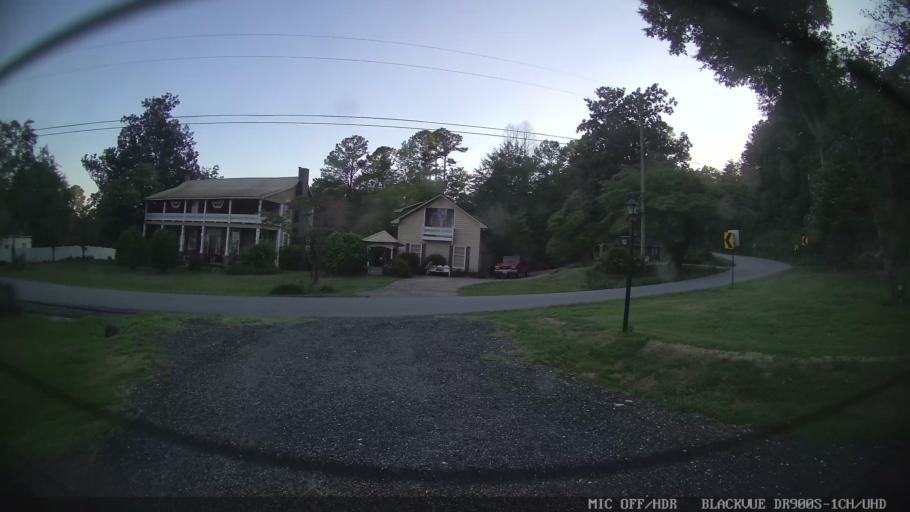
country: US
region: Georgia
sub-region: Bartow County
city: Emerson
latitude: 34.1094
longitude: -84.7125
